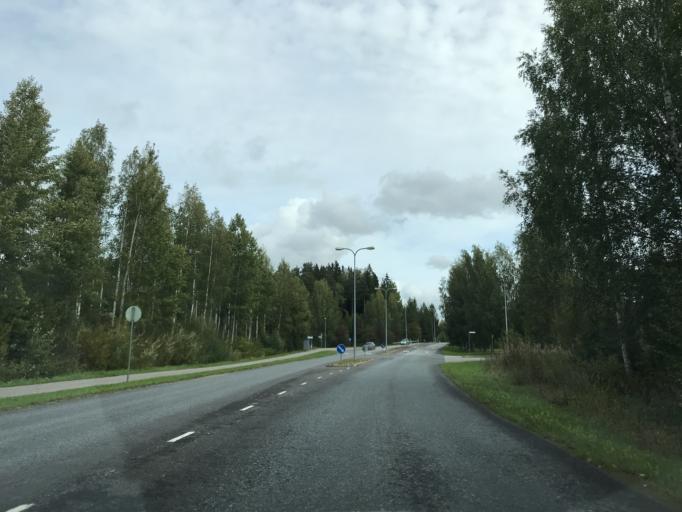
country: FI
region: Paijanne Tavastia
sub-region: Lahti
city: Lahti
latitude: 60.9968
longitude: 25.7508
